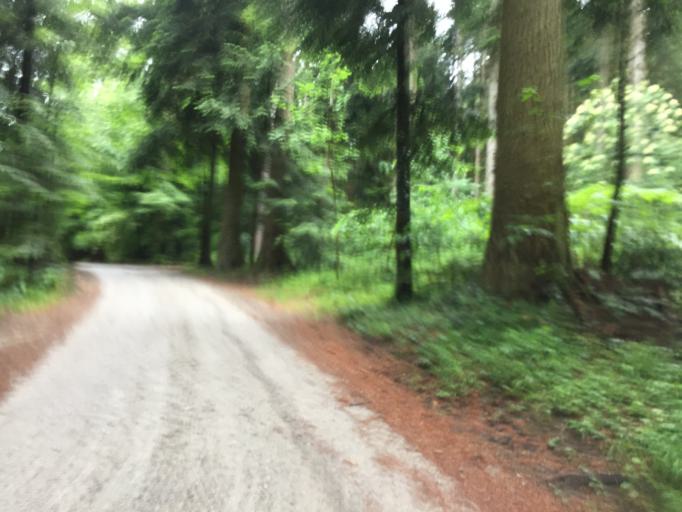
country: CH
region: Bern
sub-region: Bern-Mittelland District
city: Konolfingen
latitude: 46.8883
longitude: 7.6099
